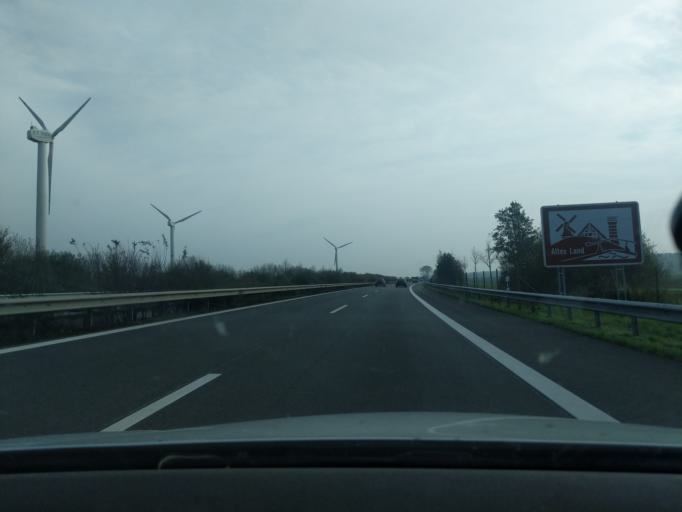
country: DE
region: Lower Saxony
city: Agathenburg
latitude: 53.5640
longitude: 9.5564
